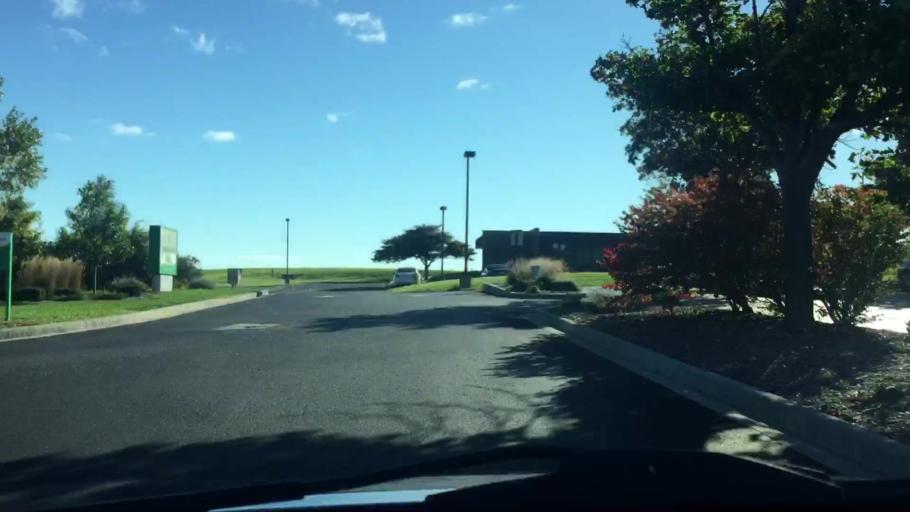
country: US
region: Wisconsin
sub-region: Waukesha County
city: Pewaukee
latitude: 43.0432
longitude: -88.2550
